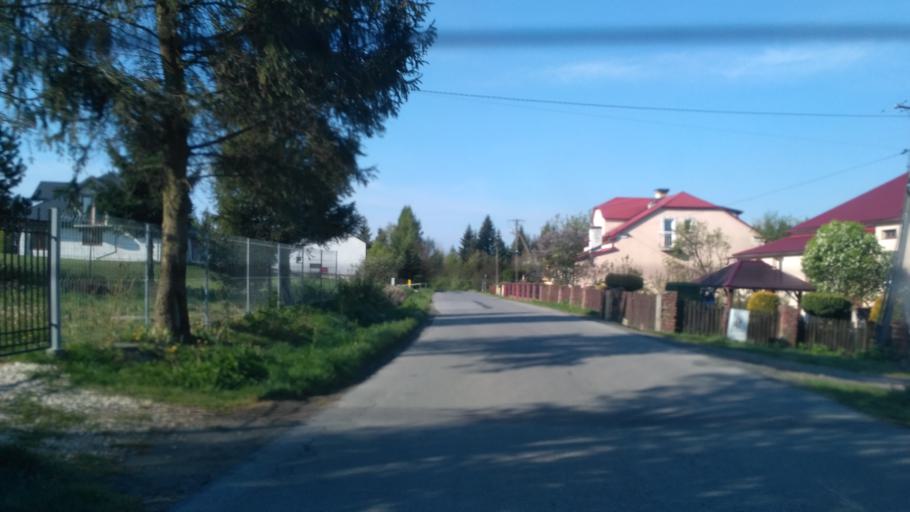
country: PL
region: Subcarpathian Voivodeship
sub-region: Powiat jaroslawski
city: Kramarzowka
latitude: 49.8448
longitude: 22.5119
